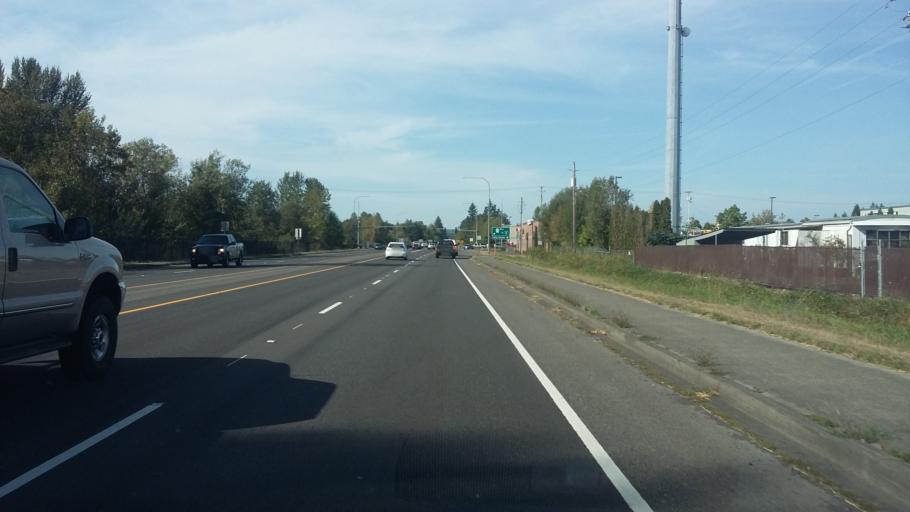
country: US
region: Washington
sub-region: Clark County
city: Battle Ground
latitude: 45.7783
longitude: -122.5475
